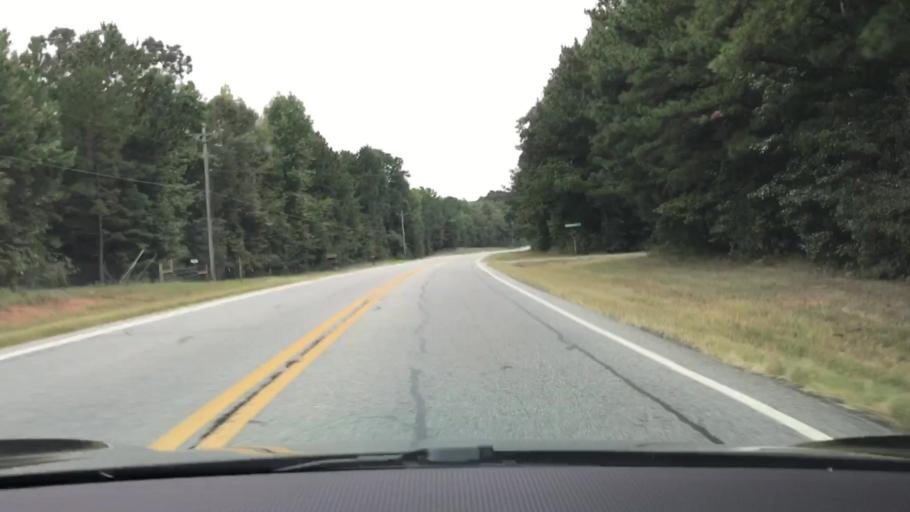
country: US
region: Georgia
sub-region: Oconee County
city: Watkinsville
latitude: 33.7596
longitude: -83.3079
